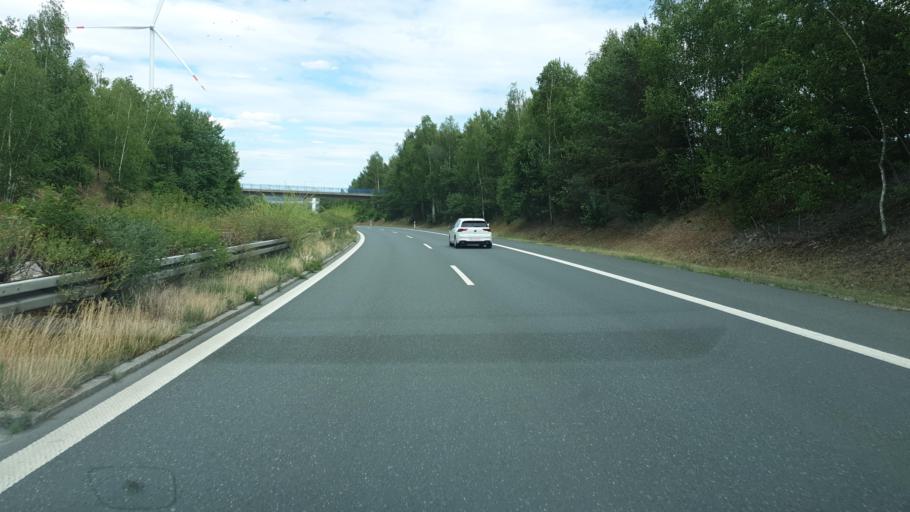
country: DE
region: Saxony
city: Dennheritz
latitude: 50.7906
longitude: 12.4641
